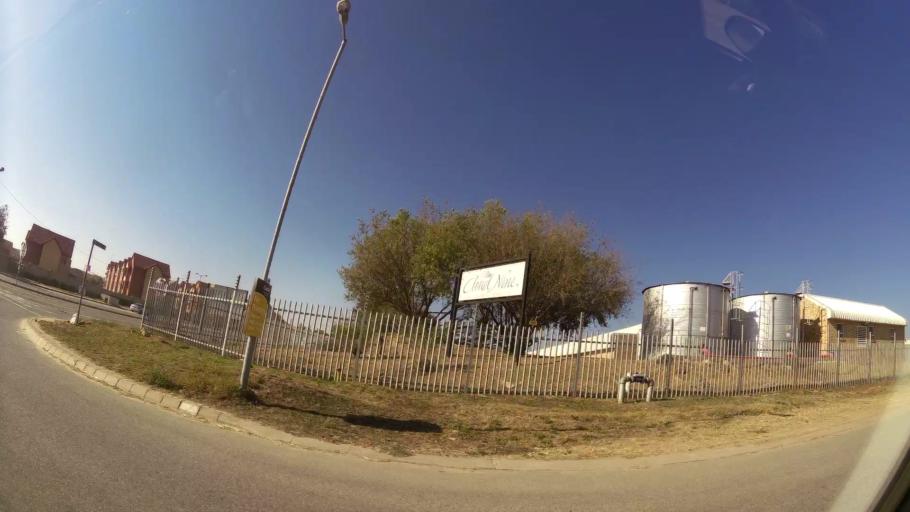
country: ZA
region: Gauteng
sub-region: City of Johannesburg Metropolitan Municipality
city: Midrand
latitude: -25.9185
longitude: 28.1269
